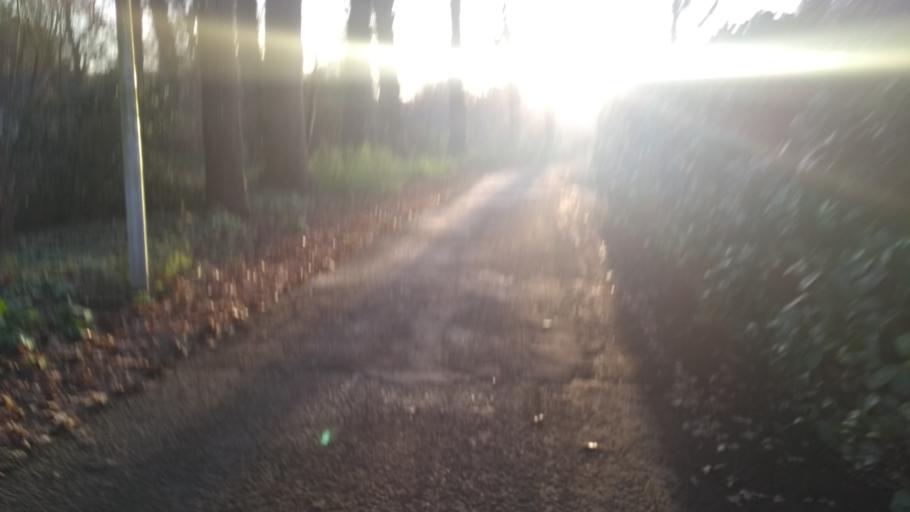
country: NL
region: Overijssel
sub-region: Gemeente Almelo
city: Almelo
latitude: 52.3719
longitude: 6.6750
